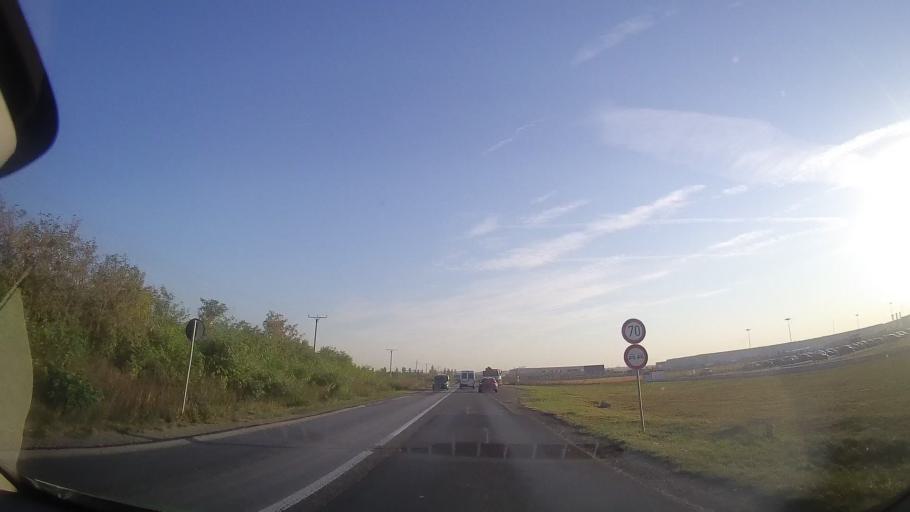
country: RO
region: Timis
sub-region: Comuna Ghiroda
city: Giarmata-Vii
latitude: 45.8254
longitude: 21.2774
